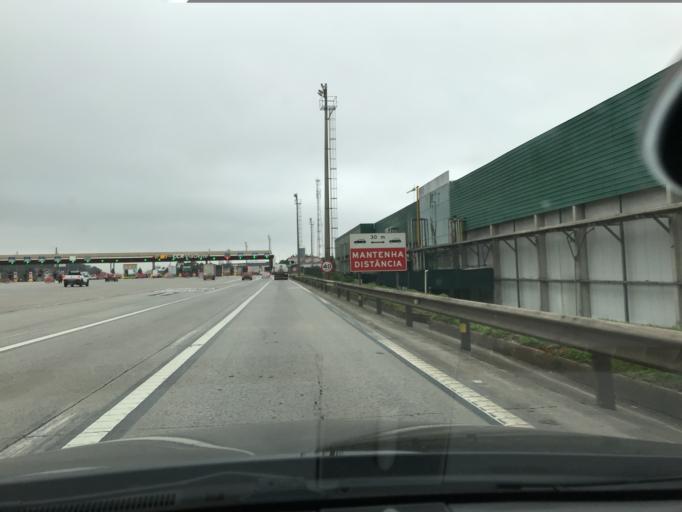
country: BR
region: Sao Paulo
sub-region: Carapicuiba
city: Carapicuiba
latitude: -23.5100
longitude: -46.8198
